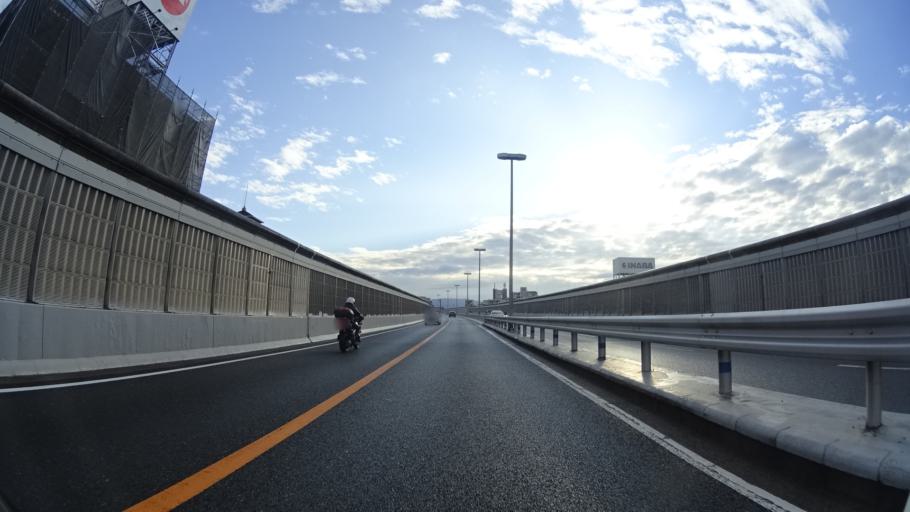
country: JP
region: Osaka
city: Moriguchi
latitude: 34.6783
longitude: 135.5691
